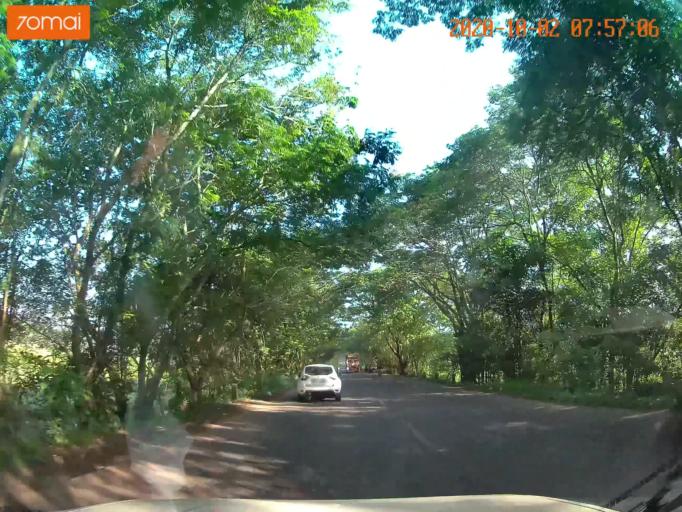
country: IN
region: Kerala
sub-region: Kozhikode
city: Ferokh
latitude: 11.1965
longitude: 75.8680
